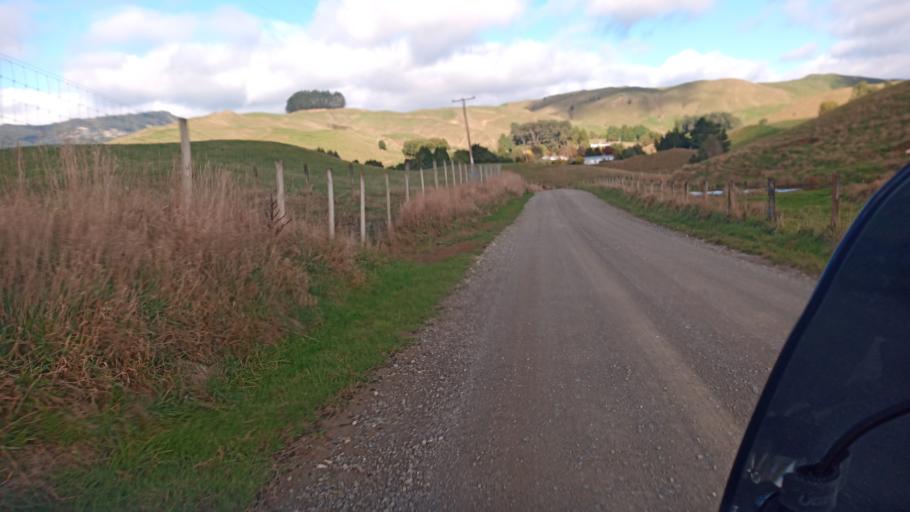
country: NZ
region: Bay of Plenty
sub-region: Opotiki District
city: Opotiki
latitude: -38.4582
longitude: 177.3903
